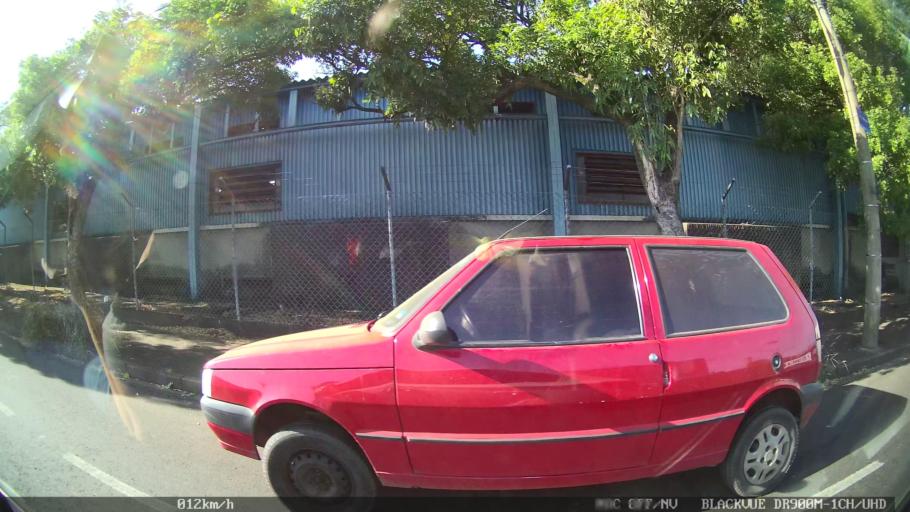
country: BR
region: Sao Paulo
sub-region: Sao Jose Do Rio Preto
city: Sao Jose do Rio Preto
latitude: -20.7868
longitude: -49.3549
